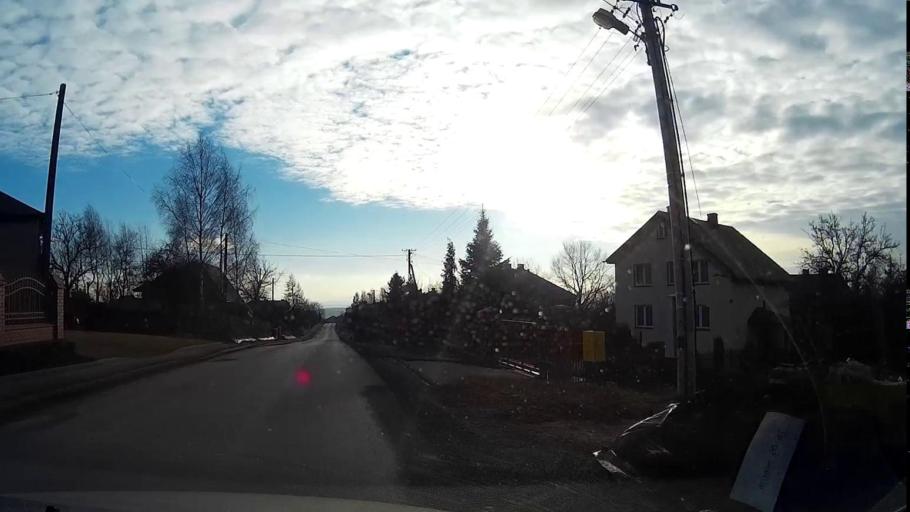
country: PL
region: Lesser Poland Voivodeship
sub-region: Powiat krakowski
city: Sanka
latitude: 50.0629
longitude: 19.6575
